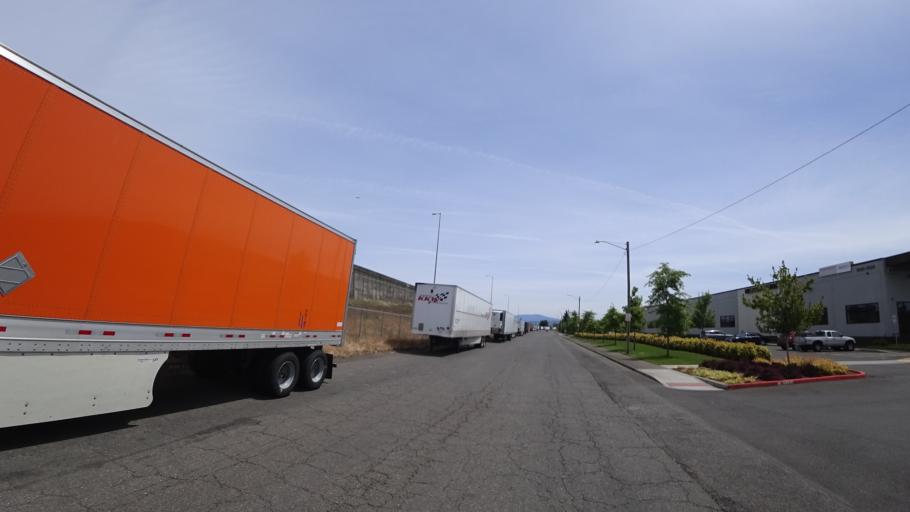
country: US
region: Oregon
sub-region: Multnomah County
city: Fairview
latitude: 45.5408
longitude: -122.4753
